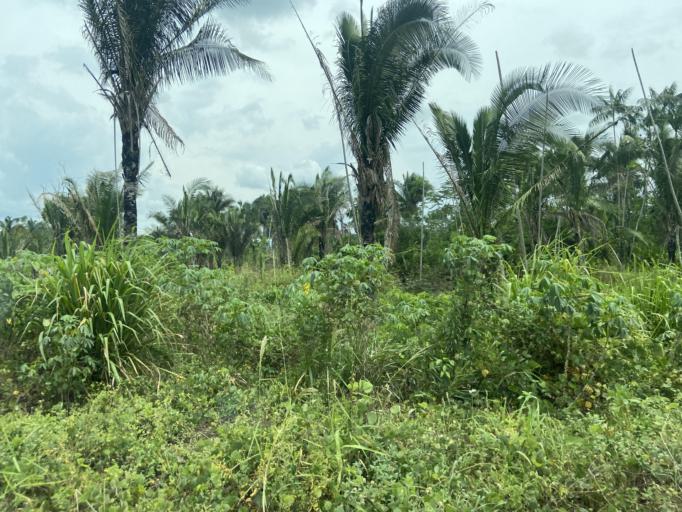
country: BR
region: Para
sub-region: Maraba
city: Maraba
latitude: -5.4241
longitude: -49.1144
